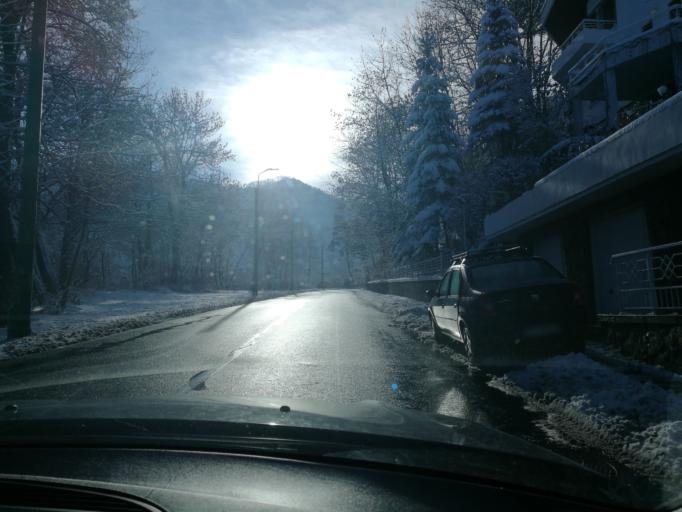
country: RO
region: Brasov
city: Brasov
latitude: 45.6443
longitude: 25.5858
